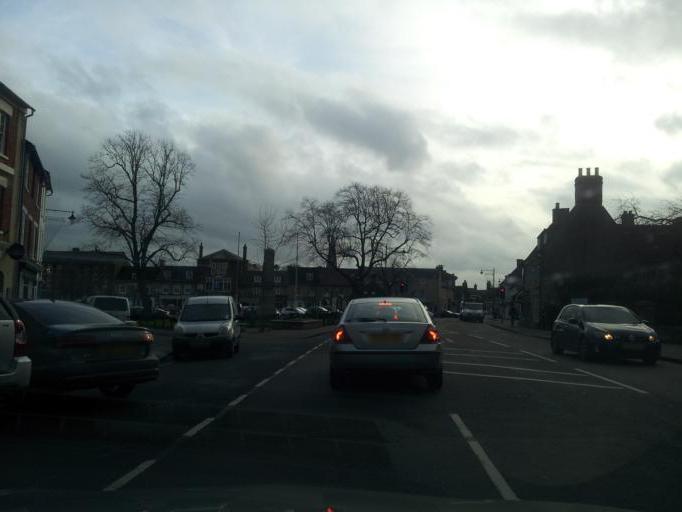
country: GB
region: England
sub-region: Milton Keynes
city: Olney
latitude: 52.1536
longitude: -0.7018
